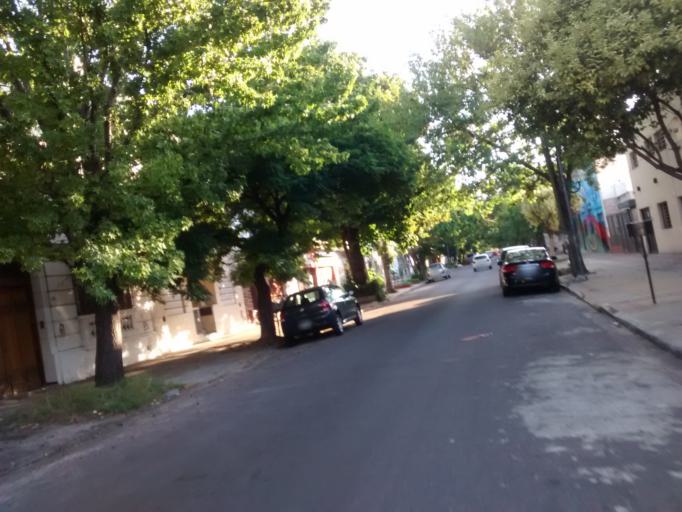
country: AR
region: Buenos Aires
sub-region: Partido de La Plata
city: La Plata
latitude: -34.9266
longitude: -57.9396
